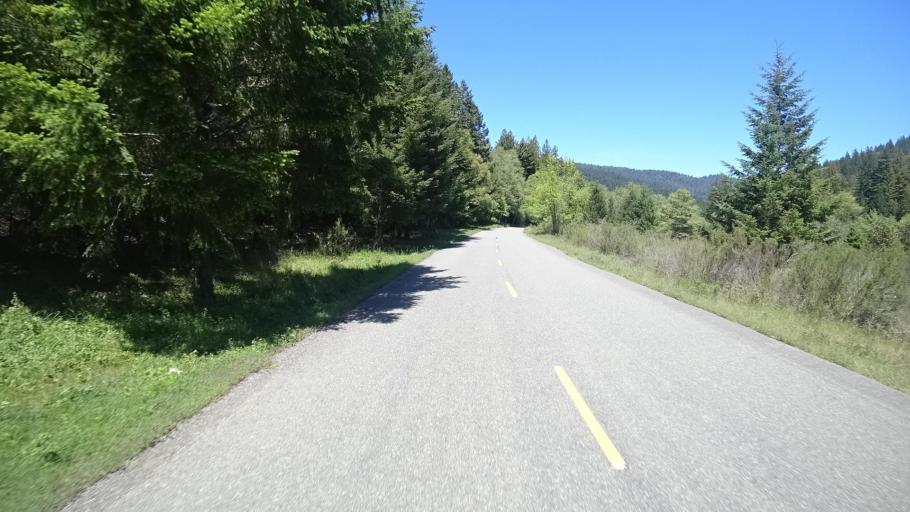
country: US
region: California
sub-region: Humboldt County
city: Rio Dell
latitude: 40.3430
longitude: -124.0269
